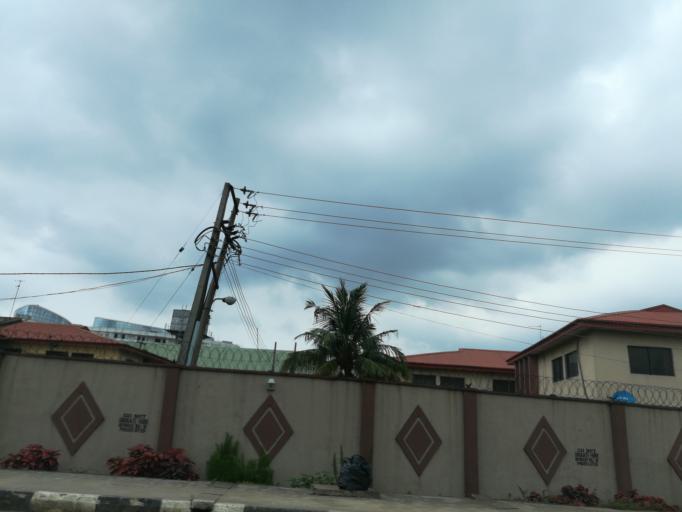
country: NG
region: Lagos
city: Ikeja
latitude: 6.6178
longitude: 3.3647
